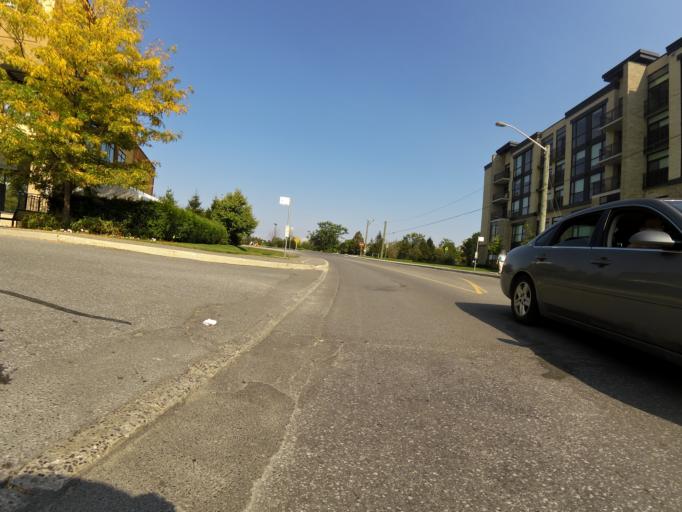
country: CA
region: Ontario
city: Bells Corners
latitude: 45.2605
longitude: -75.7675
